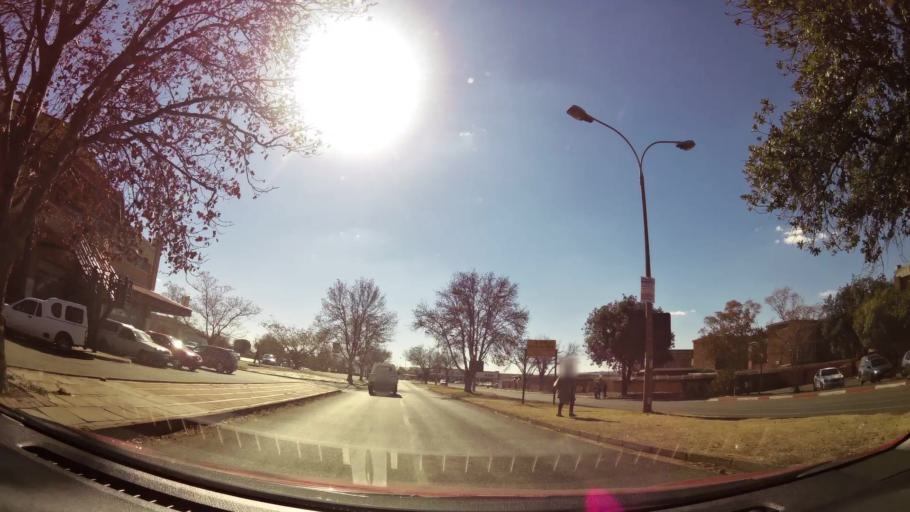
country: ZA
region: Gauteng
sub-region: West Rand District Municipality
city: Carletonville
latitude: -26.3583
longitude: 27.3966
